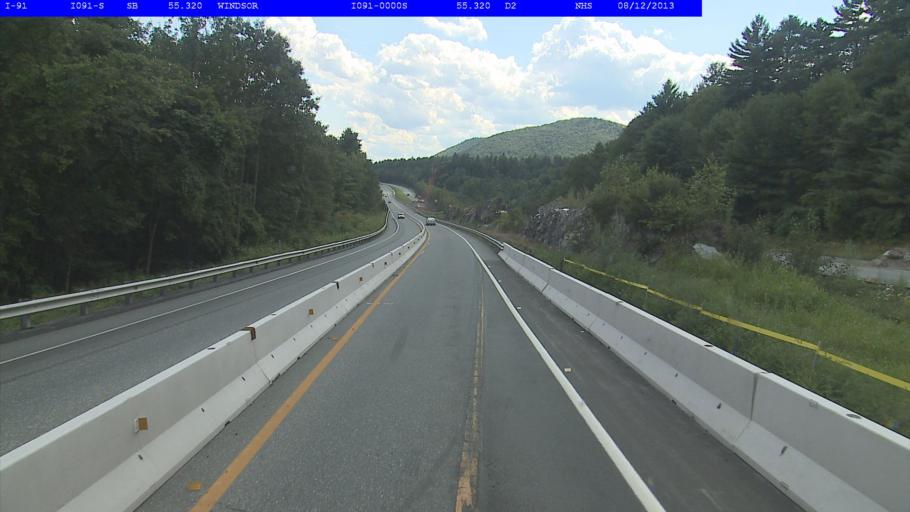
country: US
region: Vermont
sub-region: Windsor County
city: Windsor
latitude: 43.4565
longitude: -72.4066
